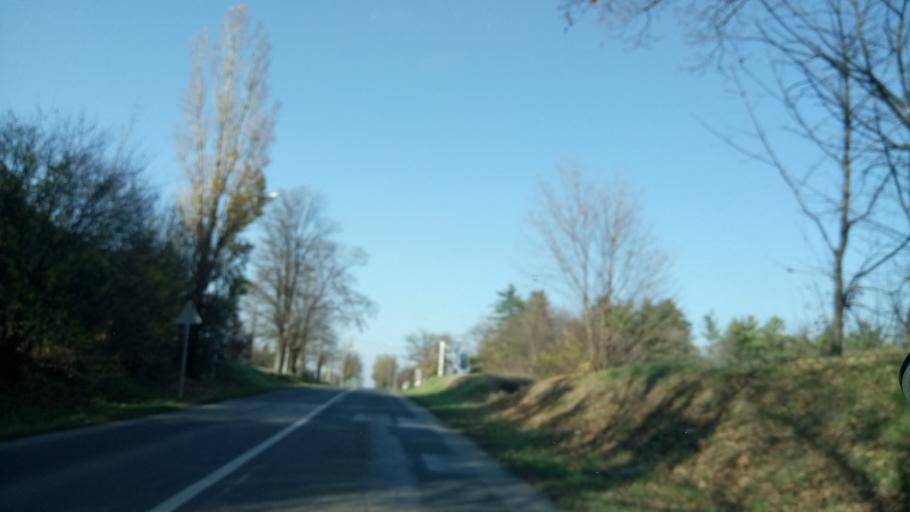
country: RS
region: Autonomna Pokrajina Vojvodina
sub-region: Sremski Okrug
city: Ingija
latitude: 45.0570
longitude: 20.0642
